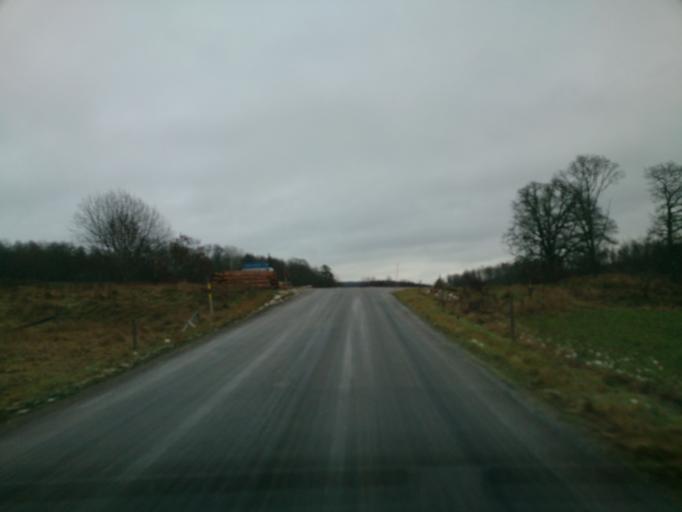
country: SE
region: OEstergoetland
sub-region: Atvidabergs Kommun
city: Atvidaberg
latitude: 58.2774
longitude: 16.1974
